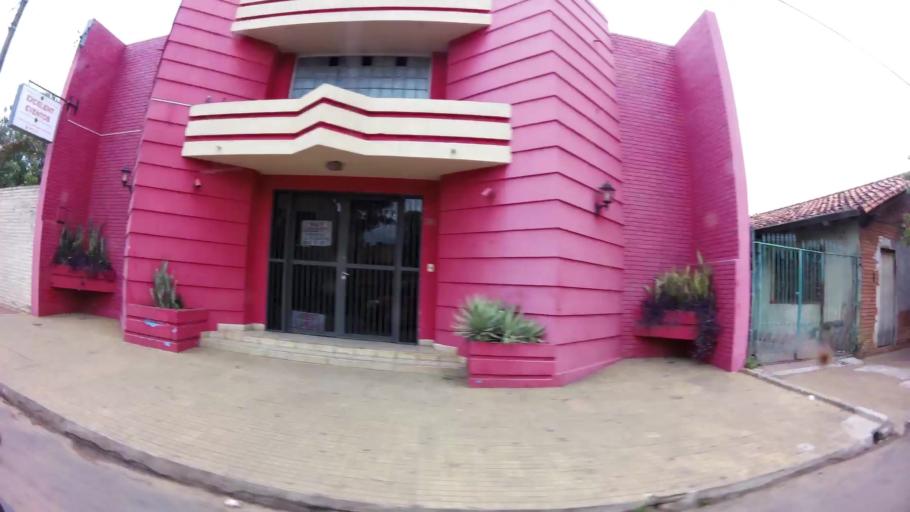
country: PY
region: Central
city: San Lorenzo
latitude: -25.2700
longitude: -57.5023
